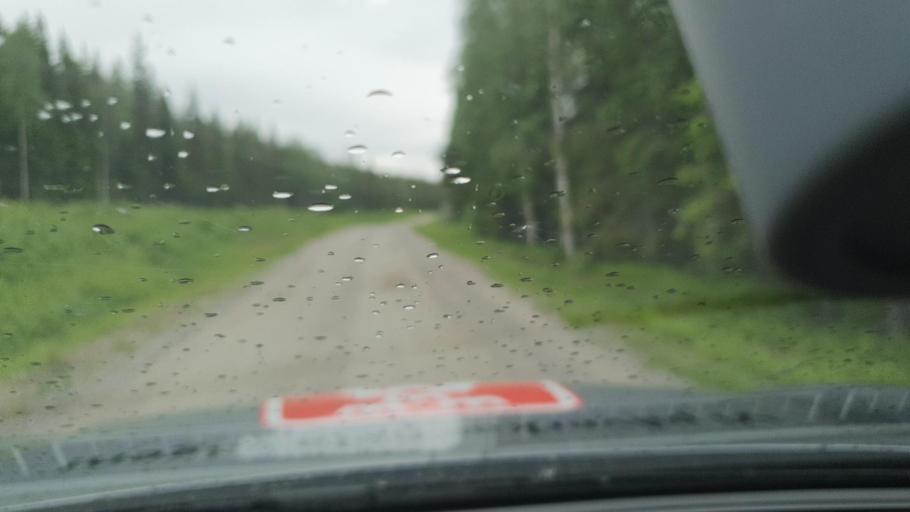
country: SE
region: Norrbotten
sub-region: Kalix Kommun
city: Rolfs
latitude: 66.0606
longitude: 23.0233
